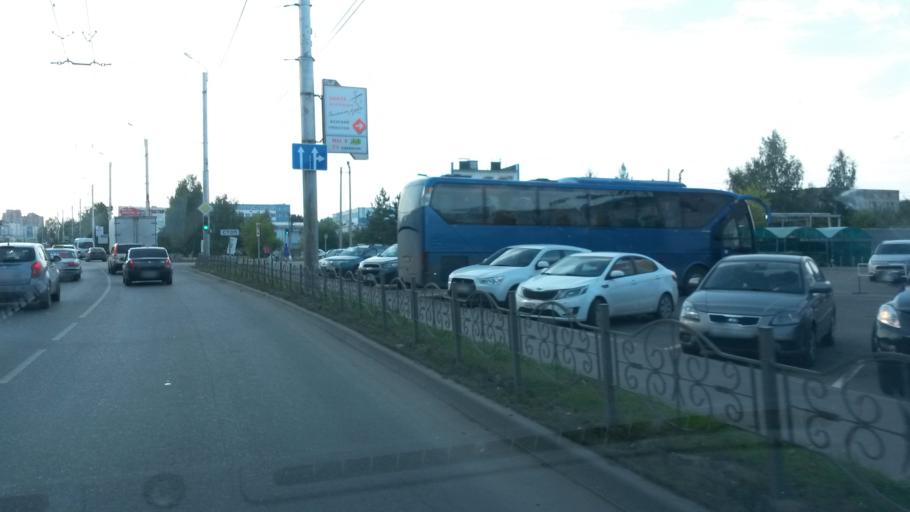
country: RU
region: Ivanovo
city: Kokhma
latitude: 56.9567
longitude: 41.0392
